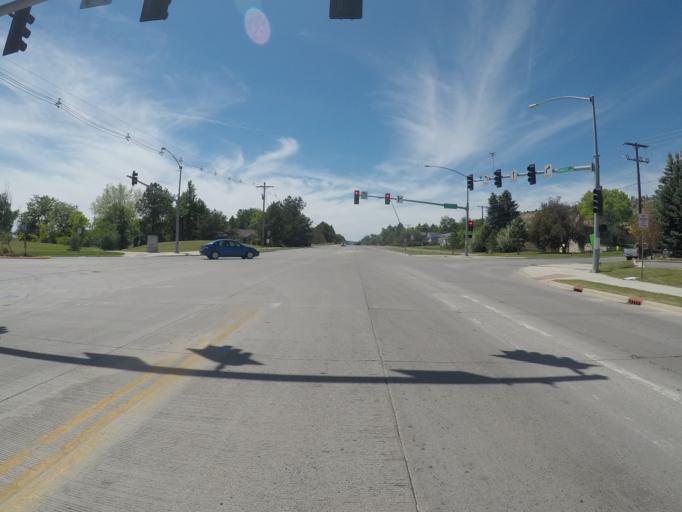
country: US
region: Montana
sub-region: Yellowstone County
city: Billings
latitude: 45.7986
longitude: -108.6176
